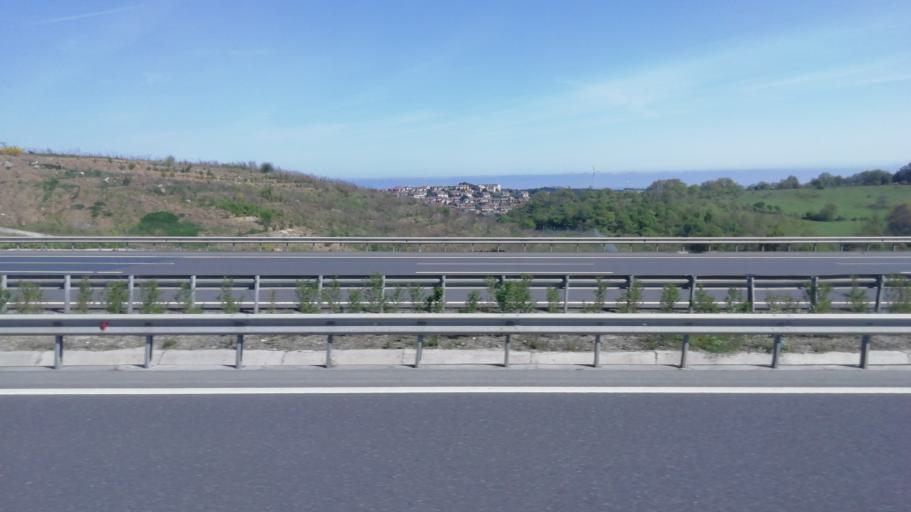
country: TR
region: Istanbul
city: Arikoey
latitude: 41.2207
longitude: 29.0033
